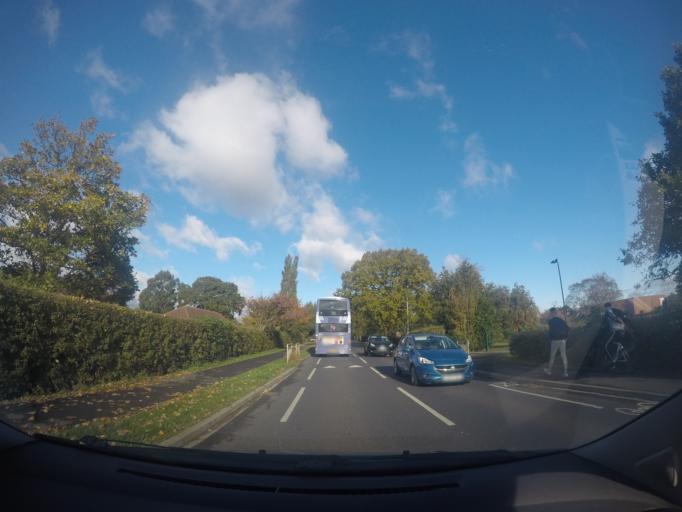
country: GB
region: England
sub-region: City of York
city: Haxby
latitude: 53.9964
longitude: -1.0717
